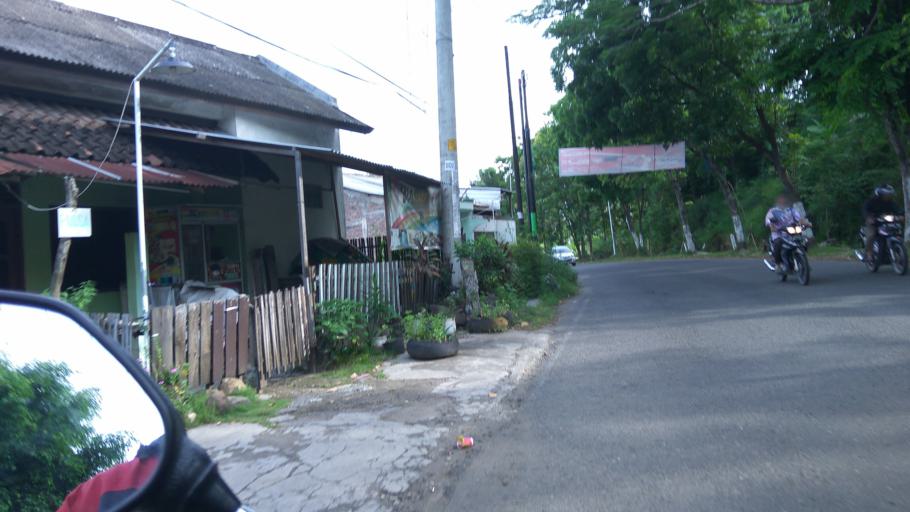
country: ID
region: Central Java
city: Semarang
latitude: -7.0354
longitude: 110.4580
